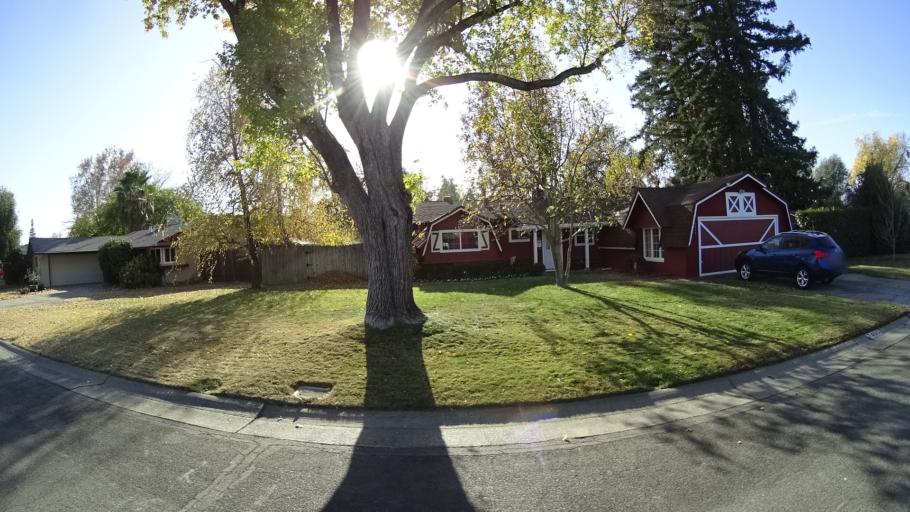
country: US
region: California
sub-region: Sacramento County
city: Antelope
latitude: 38.7033
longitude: -121.3115
